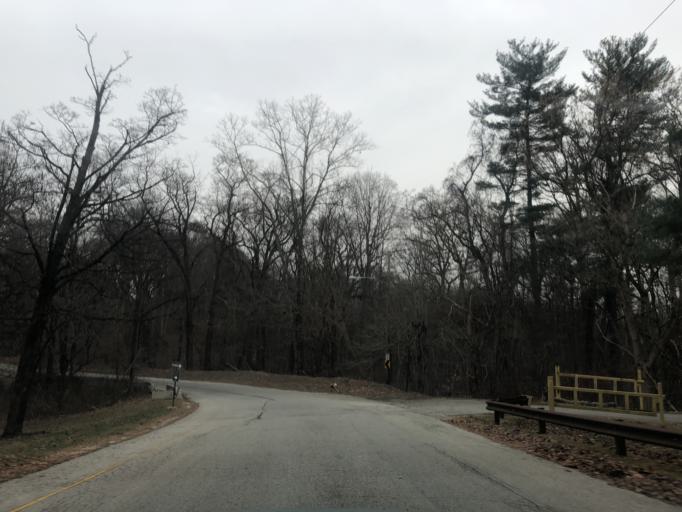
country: US
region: Pennsylvania
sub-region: Montgomery County
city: Bala-Cynwyd
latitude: 39.9961
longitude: -75.2027
